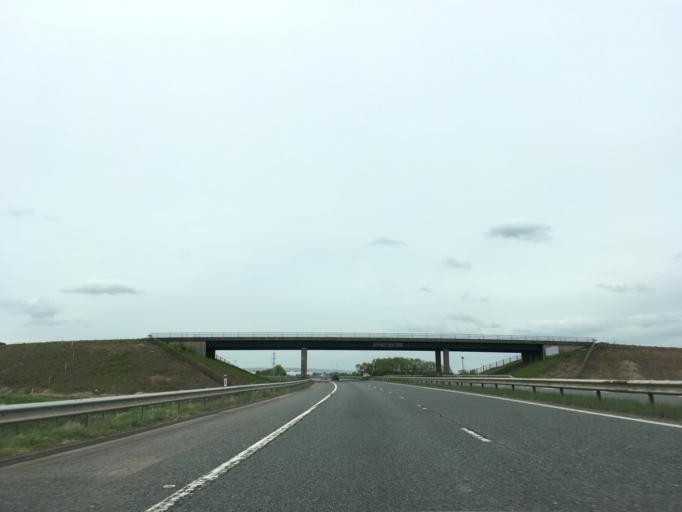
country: GB
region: England
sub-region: South Gloucestershire
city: Severn Beach
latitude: 51.5417
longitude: -2.6376
